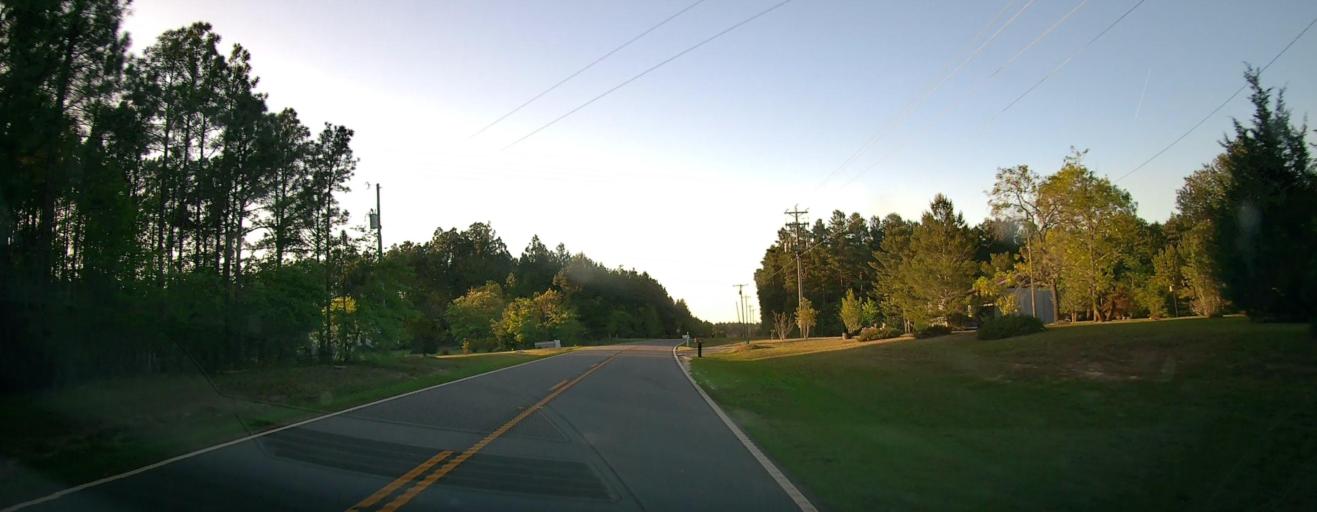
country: US
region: Georgia
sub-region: Talbot County
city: Talbotton
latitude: 32.5039
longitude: -84.4660
